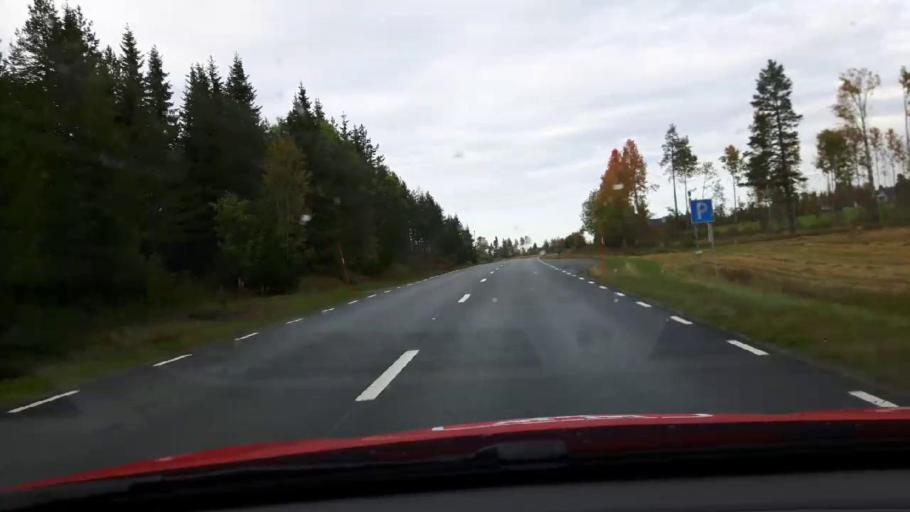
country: SE
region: Jaemtland
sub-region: Krokoms Kommun
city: Krokom
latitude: 63.1086
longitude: 14.2945
